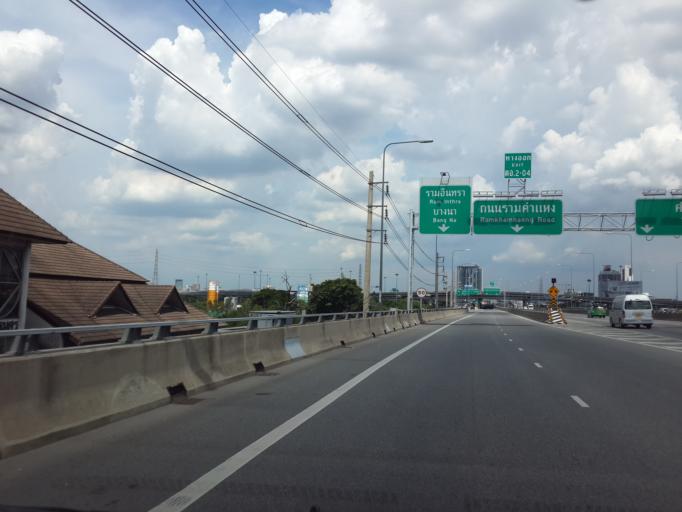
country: TH
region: Bangkok
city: Watthana
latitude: 13.7530
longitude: 100.5896
